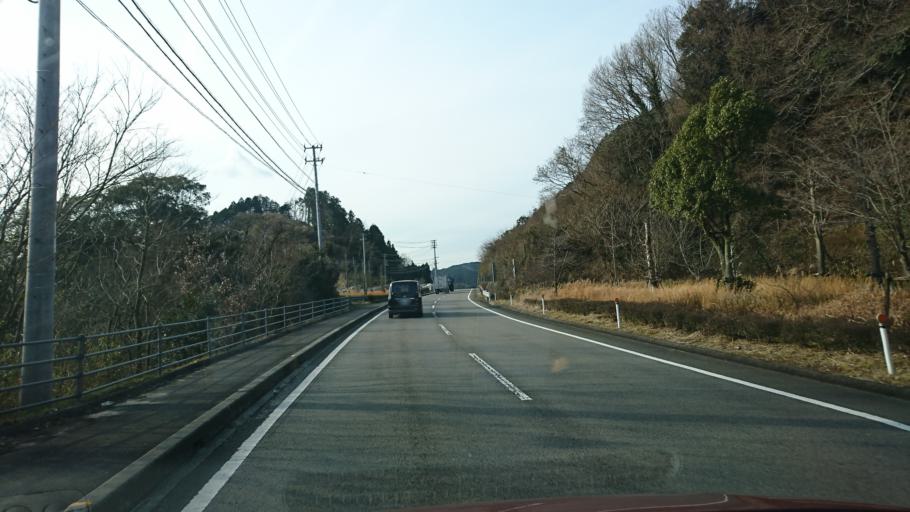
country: JP
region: Ehime
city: Hojo
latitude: 33.9941
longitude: 132.9288
